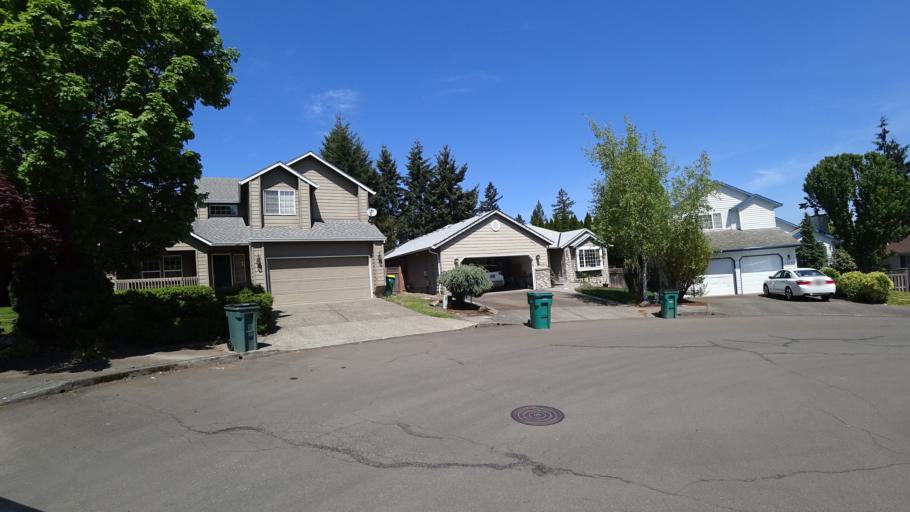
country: US
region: Oregon
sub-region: Washington County
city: King City
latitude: 45.4311
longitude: -122.8221
